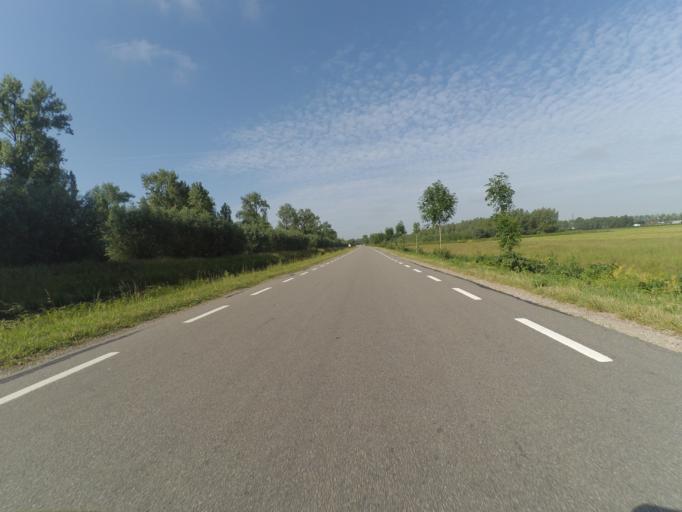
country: NL
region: Gelderland
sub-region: Gemeente Culemborg
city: Culemborg
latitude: 51.9325
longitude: 5.2505
